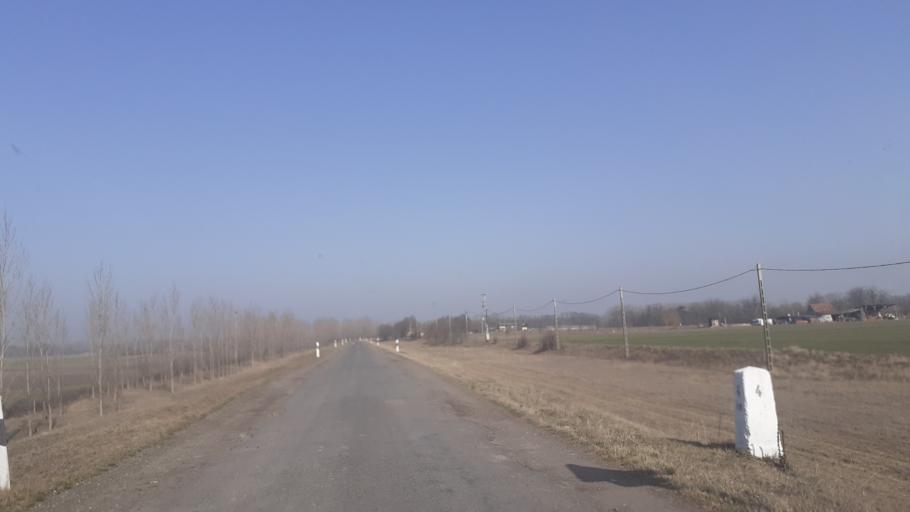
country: HU
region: Pest
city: Domsod
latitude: 47.0646
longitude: 18.9989
